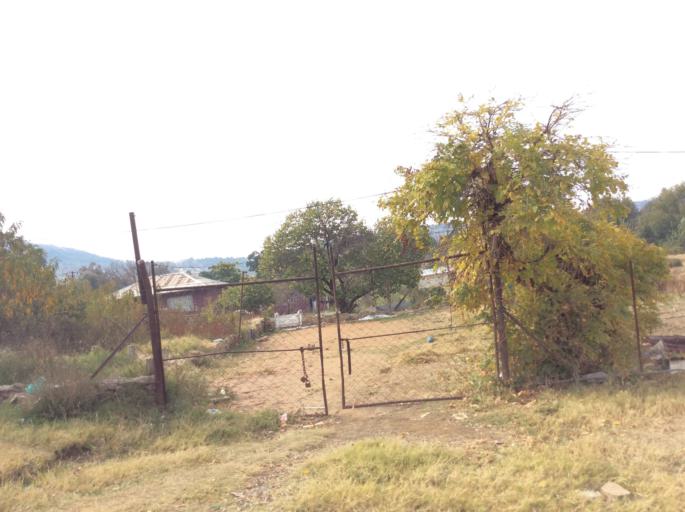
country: LS
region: Mafeteng
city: Mafeteng
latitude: -29.7254
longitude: 27.0325
